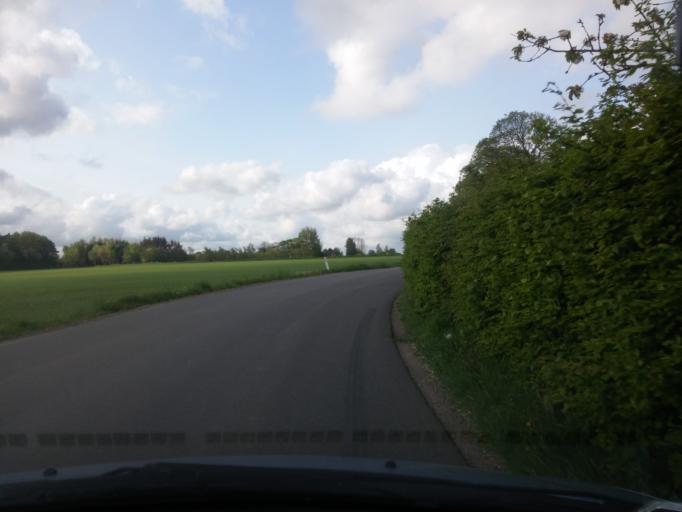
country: DK
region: South Denmark
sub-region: Kerteminde Kommune
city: Langeskov
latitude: 55.4007
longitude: 10.5960
